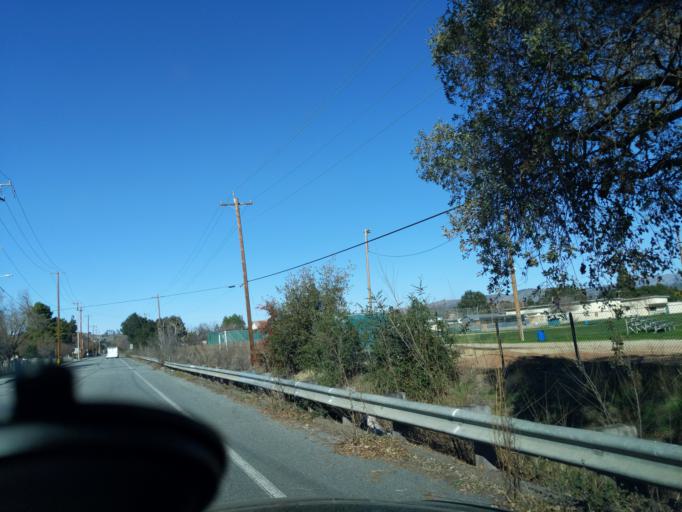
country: US
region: California
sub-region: Santa Clara County
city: Morgan Hill
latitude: 37.1291
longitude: -121.6591
